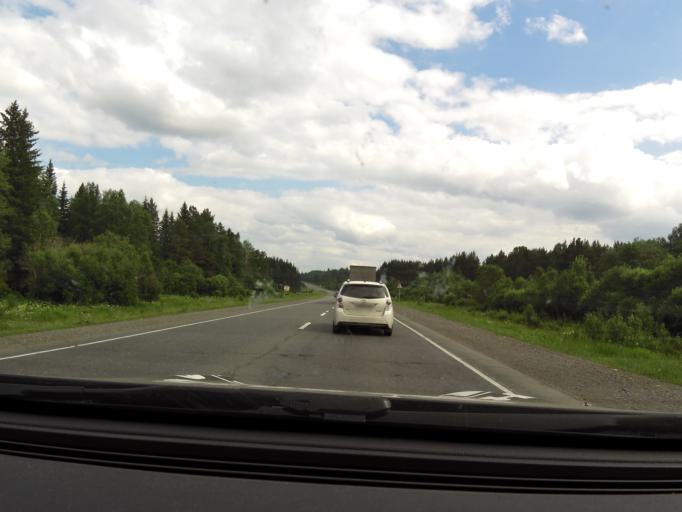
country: RU
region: Sverdlovsk
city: Atig
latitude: 56.8059
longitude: 59.3720
